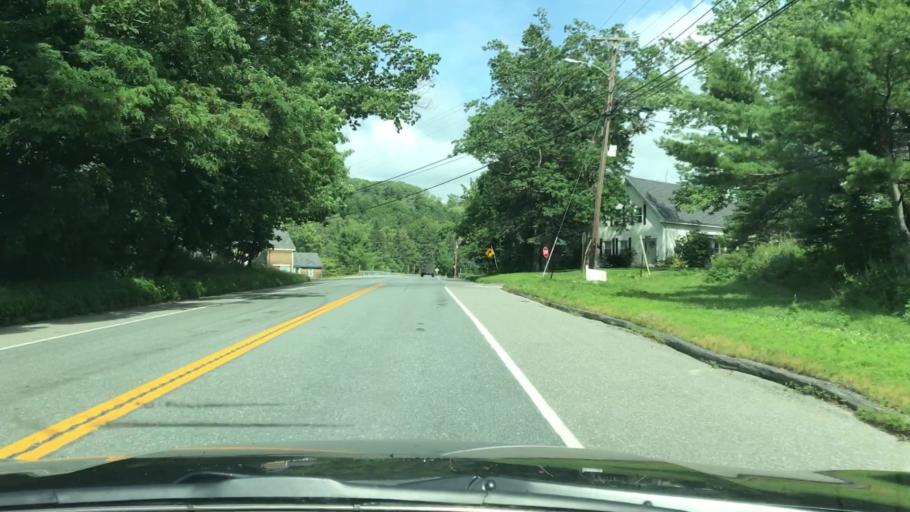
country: US
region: Maine
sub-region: Hancock County
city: Orland
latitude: 44.5673
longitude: -68.6798
